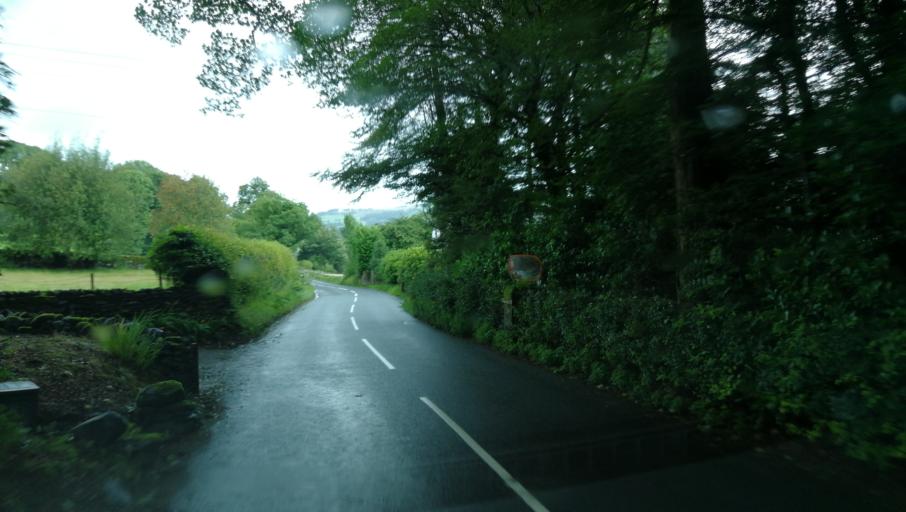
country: GB
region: England
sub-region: Cumbria
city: Penrith
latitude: 54.5888
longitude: -2.8627
